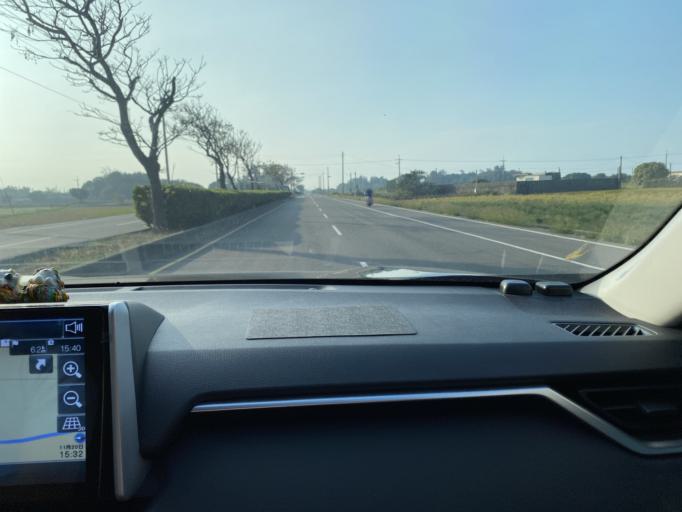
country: TW
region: Taiwan
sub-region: Changhua
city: Chang-hua
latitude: 23.9594
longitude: 120.3985
